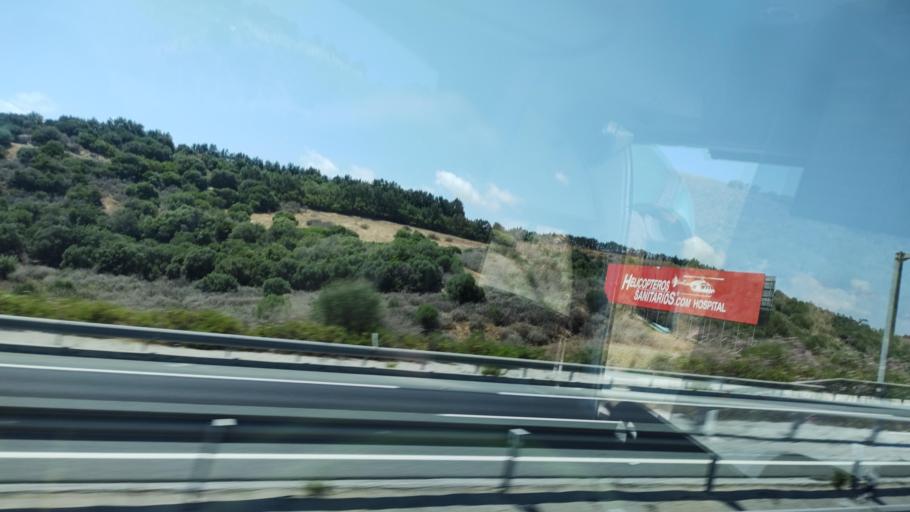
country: ES
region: Andalusia
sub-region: Provincia de Malaga
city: Manilva
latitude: 36.3036
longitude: -5.2787
